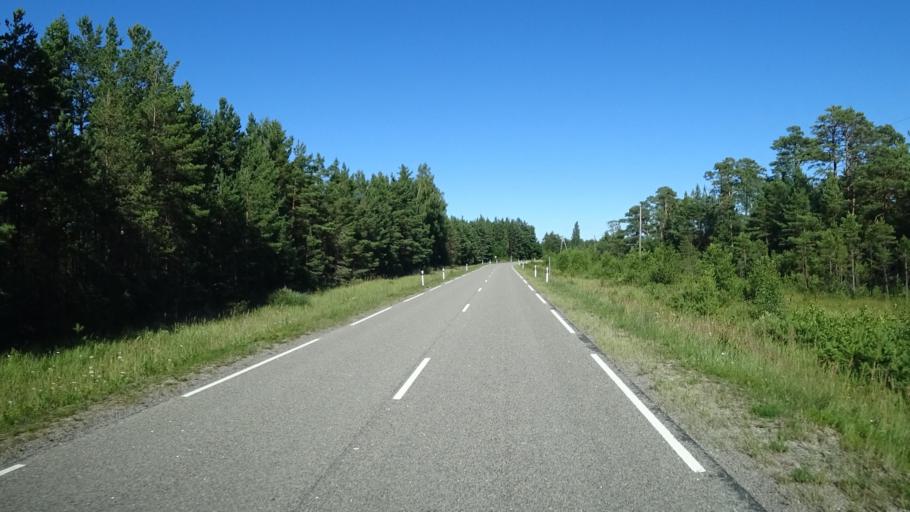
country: LV
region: Dundaga
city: Dundaga
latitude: 57.6977
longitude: 22.4069
